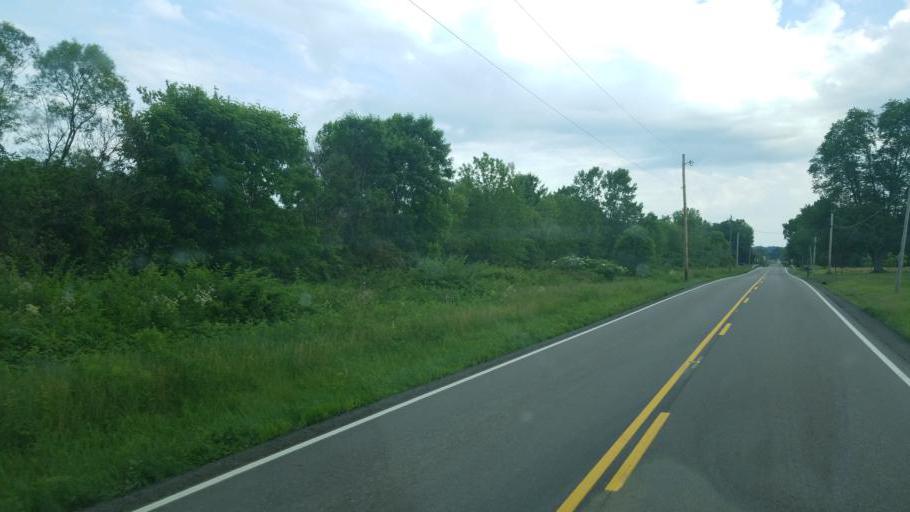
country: US
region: Ohio
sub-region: Knox County
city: Danville
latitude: 40.5035
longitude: -82.2868
